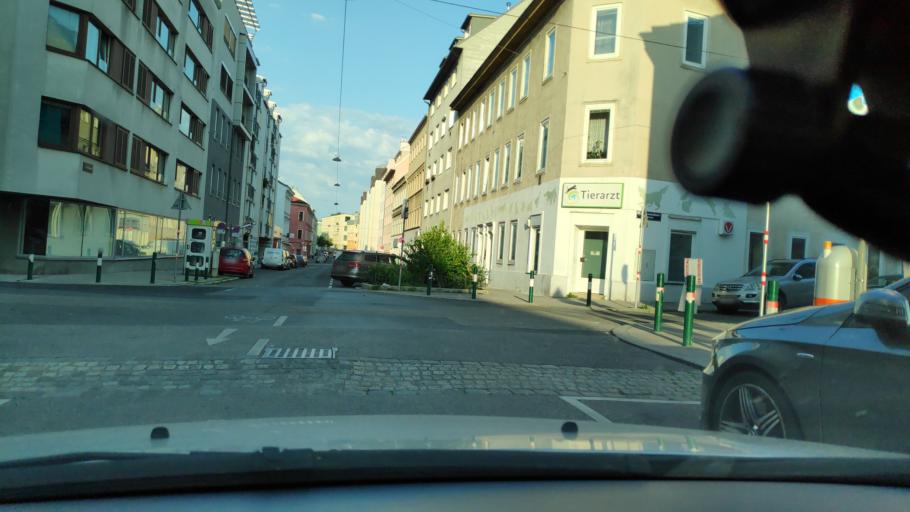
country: AT
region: Vienna
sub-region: Wien Stadt
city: Vienna
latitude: 48.2169
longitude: 16.3241
